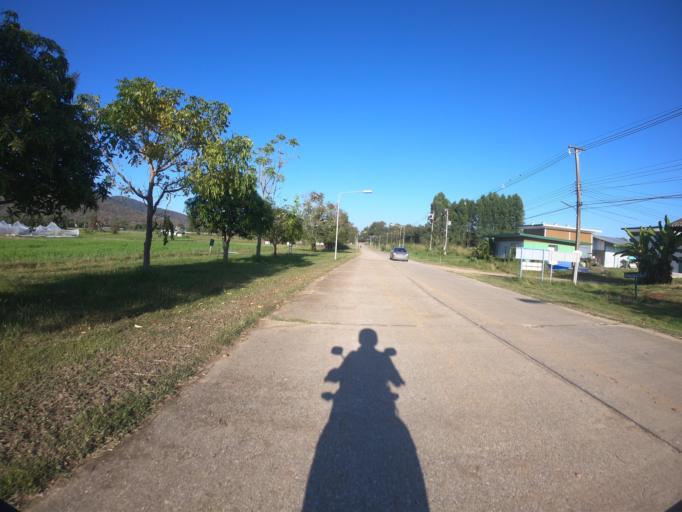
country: TH
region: Chiang Mai
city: Chiang Mai
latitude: 18.7582
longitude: 98.9297
